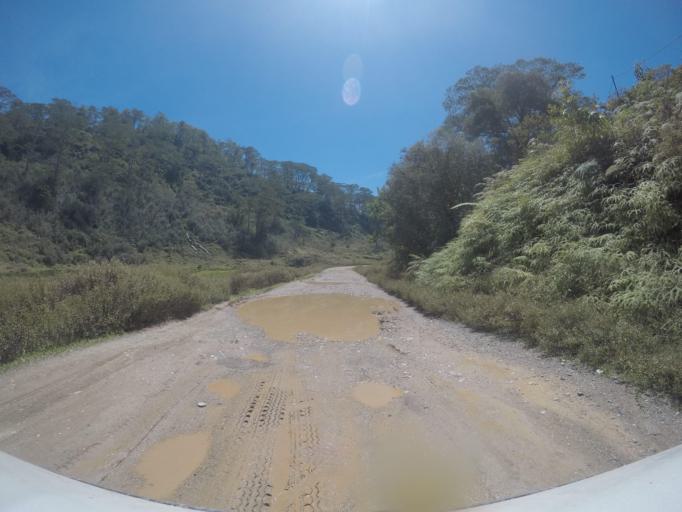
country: TL
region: Ermera
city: Gleno
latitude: -8.7751
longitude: 125.3931
